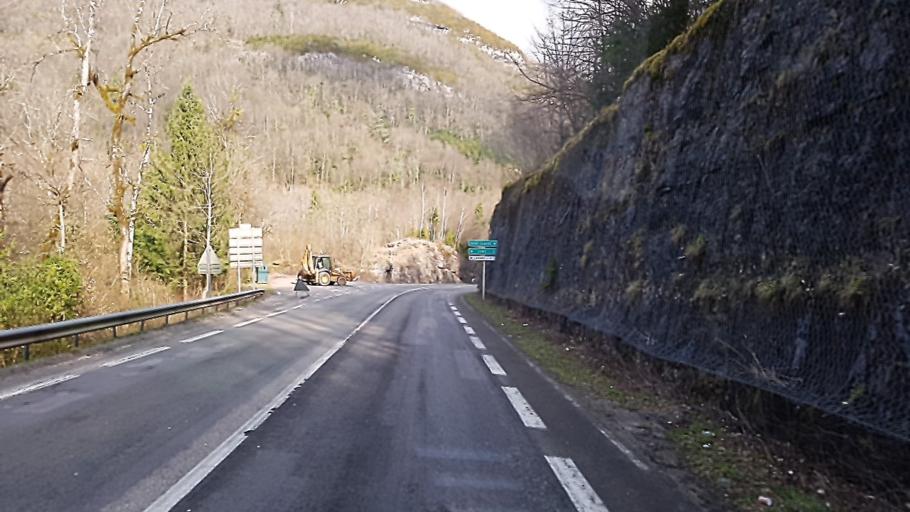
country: FR
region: Franche-Comte
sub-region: Departement du Jura
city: Lavans-les-Saint-Claude
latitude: 46.3816
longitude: 5.8008
